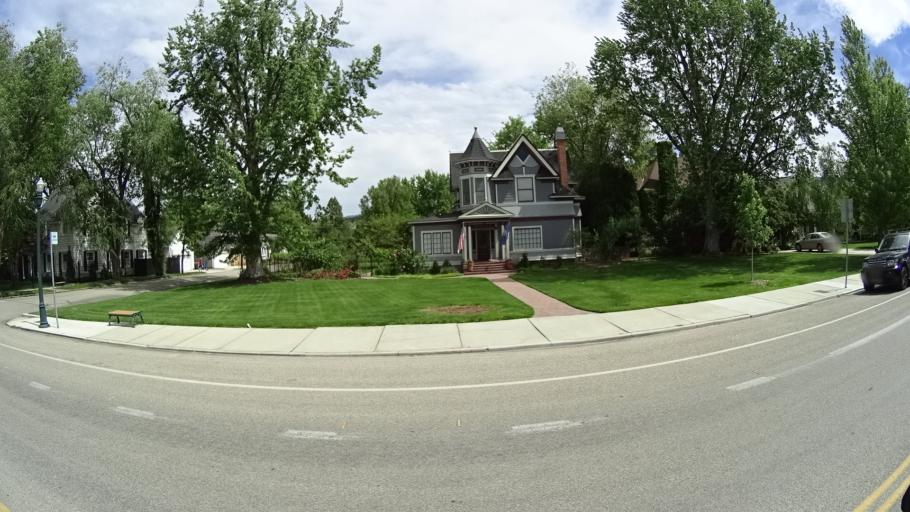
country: US
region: Idaho
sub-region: Ada County
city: Boise
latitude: 43.6048
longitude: -116.1773
